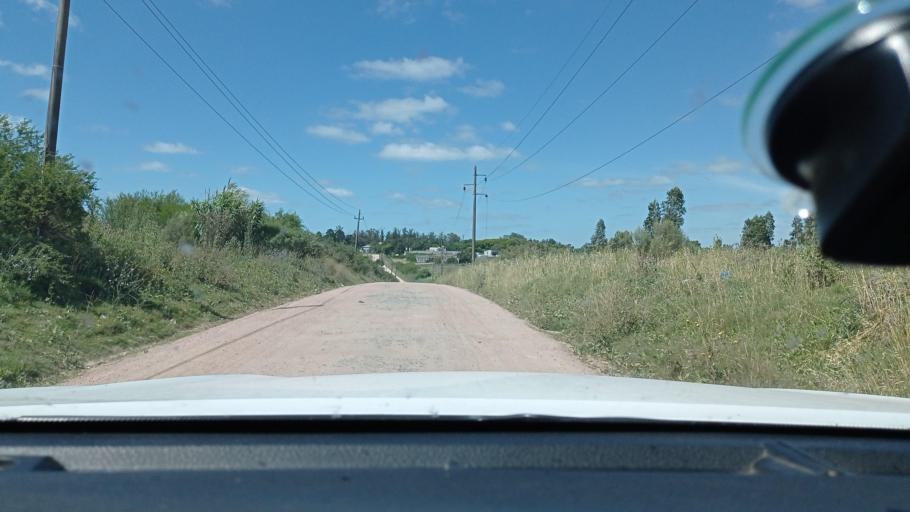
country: UY
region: Canelones
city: Pando
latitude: -34.7274
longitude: -55.9739
